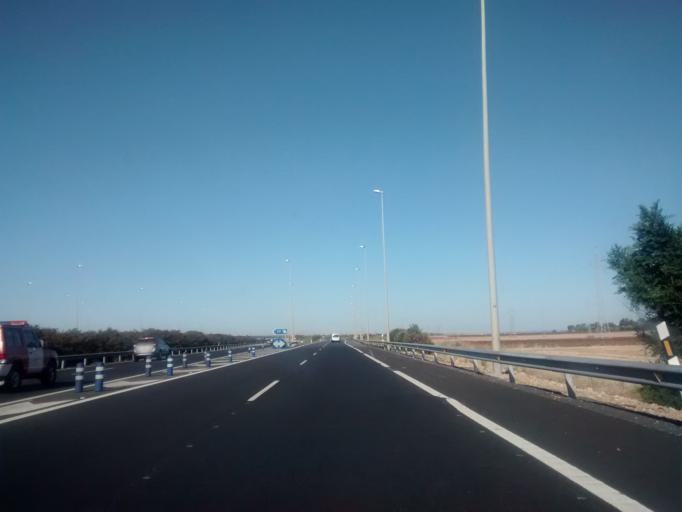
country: ES
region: Andalusia
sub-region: Provincia de Huelva
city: San Juan del Puerto
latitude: 37.3151
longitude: -6.8695
